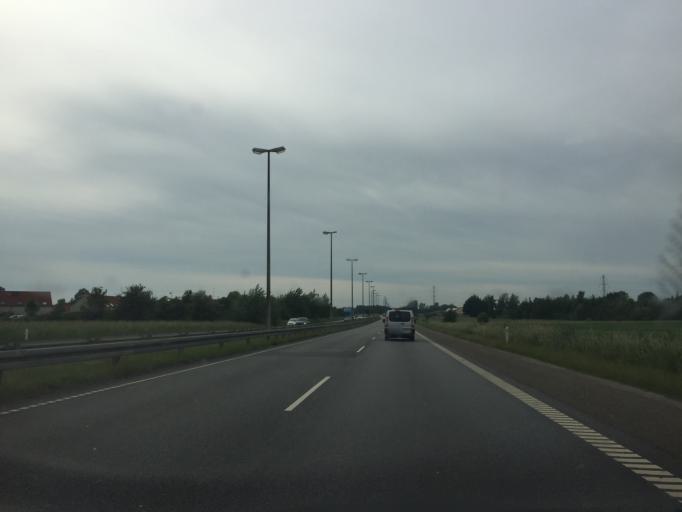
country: DK
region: Capital Region
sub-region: Hoje-Taastrup Kommune
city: Taastrup
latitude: 55.6263
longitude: 12.3108
